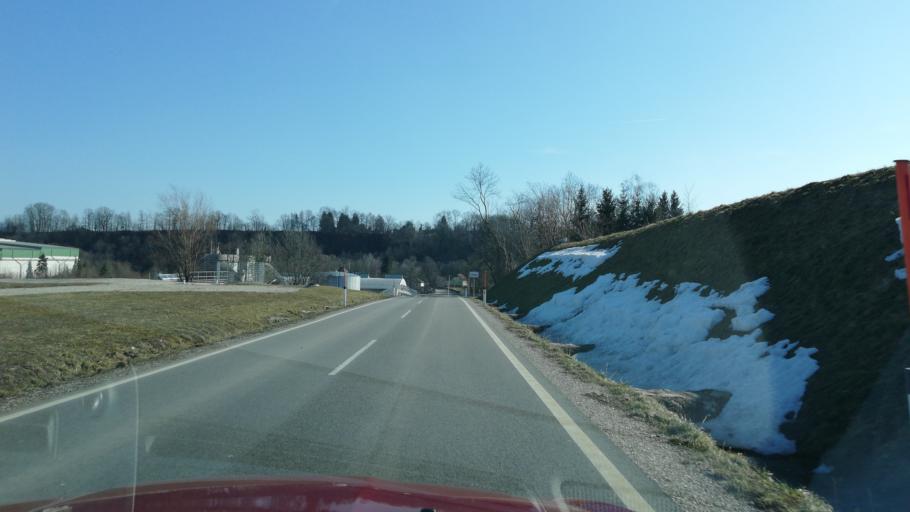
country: AT
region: Upper Austria
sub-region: Politischer Bezirk Vocklabruck
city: Redlham
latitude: 48.0157
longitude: 13.7443
